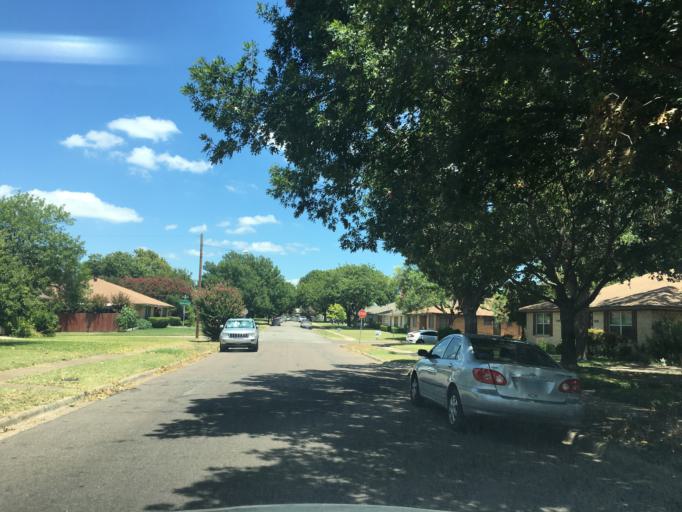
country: US
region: Texas
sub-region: Dallas County
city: Garland
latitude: 32.8516
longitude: -96.6870
